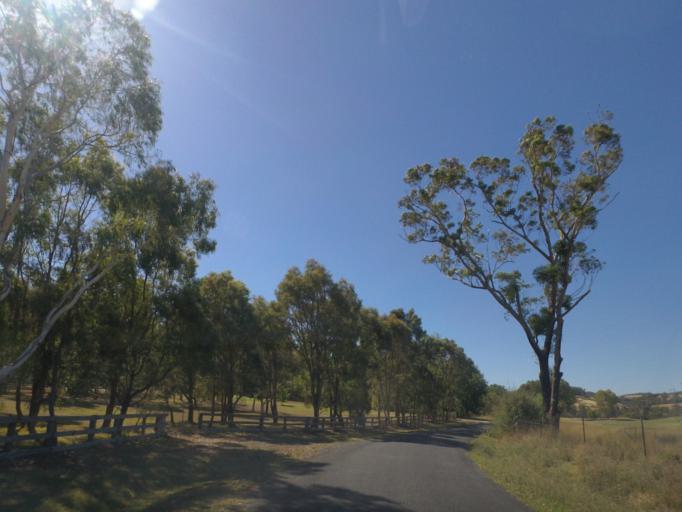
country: AU
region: Victoria
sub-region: Yarra Ranges
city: Chirnside Park
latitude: -37.7195
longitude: 145.2925
